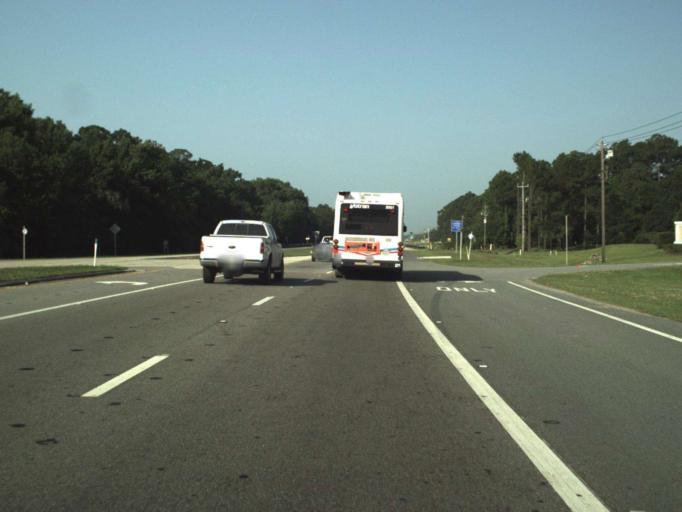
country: US
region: Florida
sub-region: Volusia County
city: Daytona Beach
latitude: 29.1657
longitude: -81.0887
